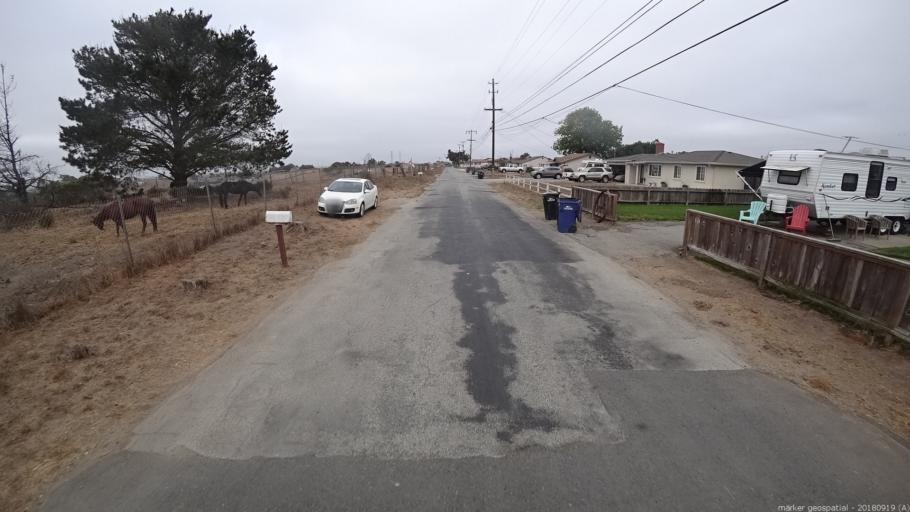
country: US
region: California
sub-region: Monterey County
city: Elkhorn
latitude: 36.7992
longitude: -121.7226
